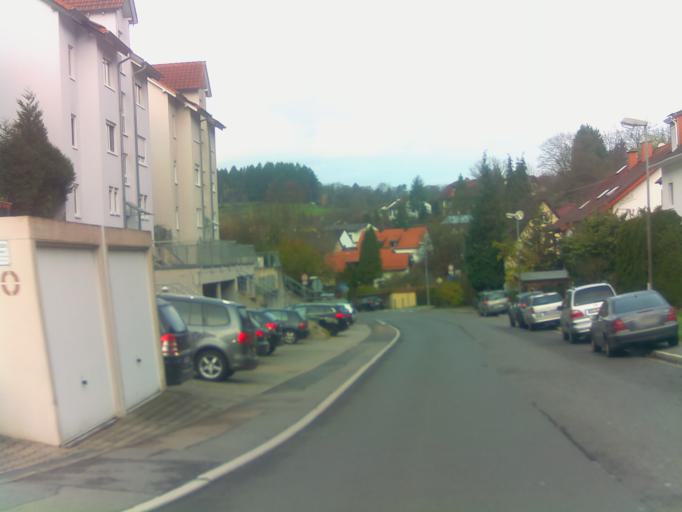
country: DE
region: Baden-Wuerttemberg
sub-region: Karlsruhe Region
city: Wilhelmsfeld
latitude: 49.4844
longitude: 8.7432
